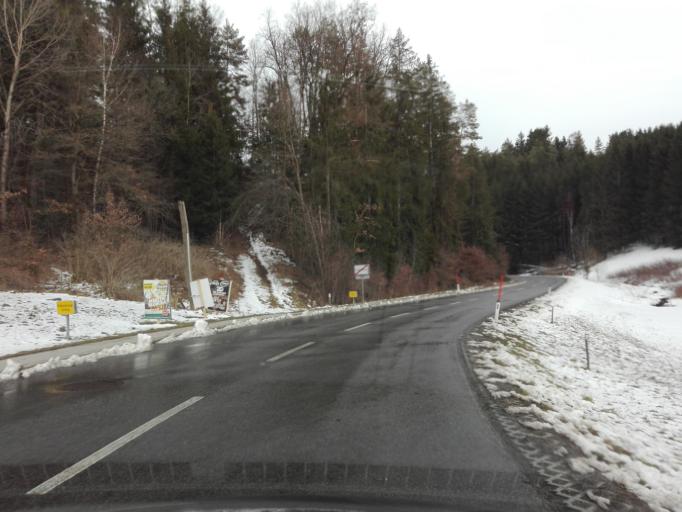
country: AT
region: Upper Austria
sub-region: Politischer Bezirk Rohrbach
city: Atzesberg
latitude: 48.5503
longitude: 13.9055
